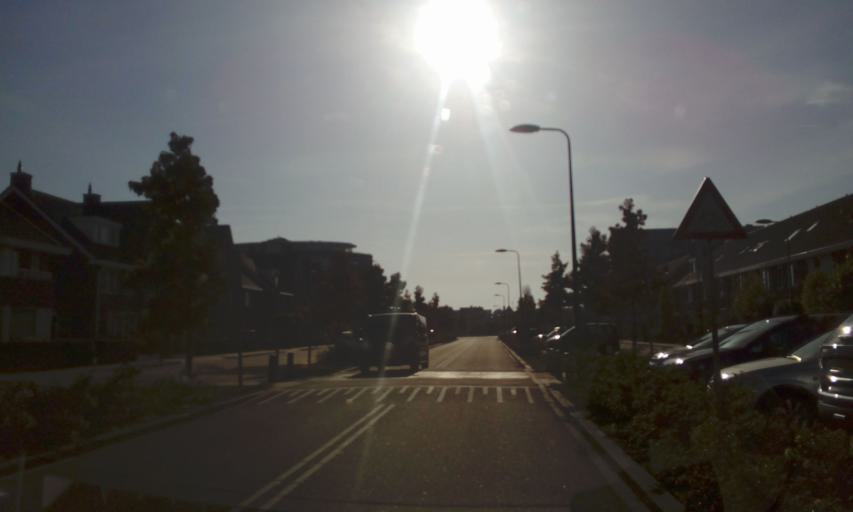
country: NL
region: South Holland
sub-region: Gemeente Lansingerland
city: Bleiswijk
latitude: 52.0115
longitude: 4.5356
